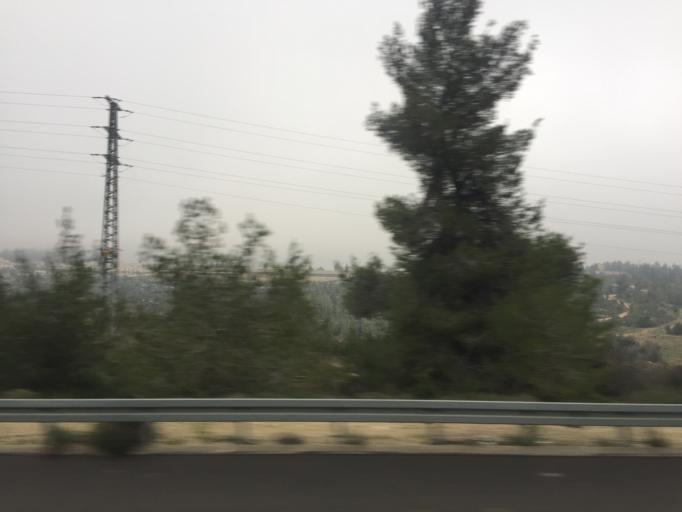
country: IL
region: Jerusalem
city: Abu Ghaush
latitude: 31.8008
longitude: 35.0881
